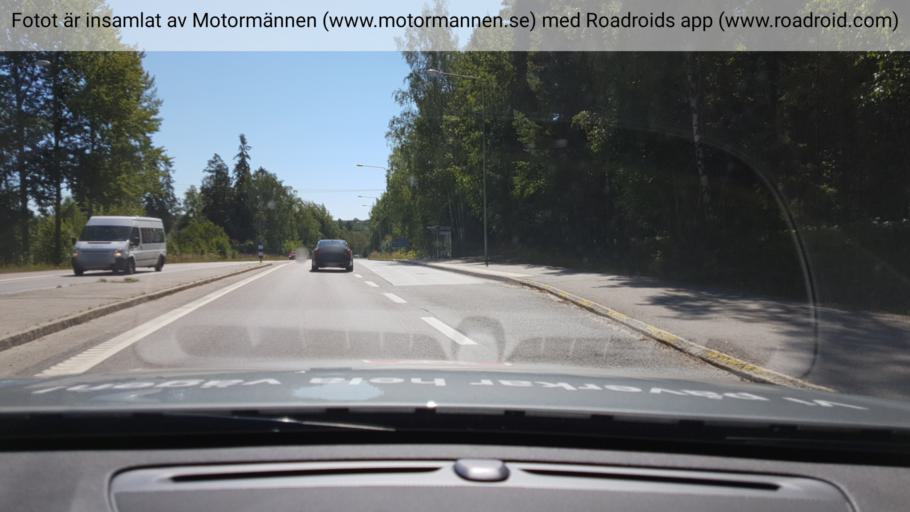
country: SE
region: Stockholm
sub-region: Nacka Kommun
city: Alta
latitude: 59.2335
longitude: 18.1929
